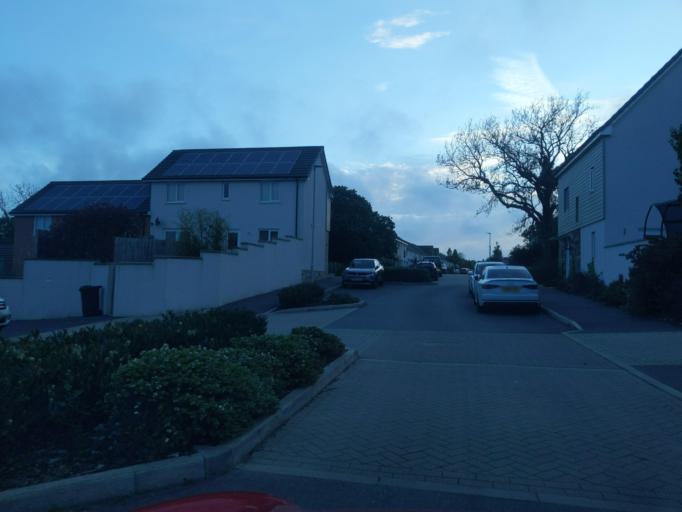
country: GB
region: England
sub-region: Plymouth
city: Plymouth
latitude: 50.4097
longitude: -4.1162
